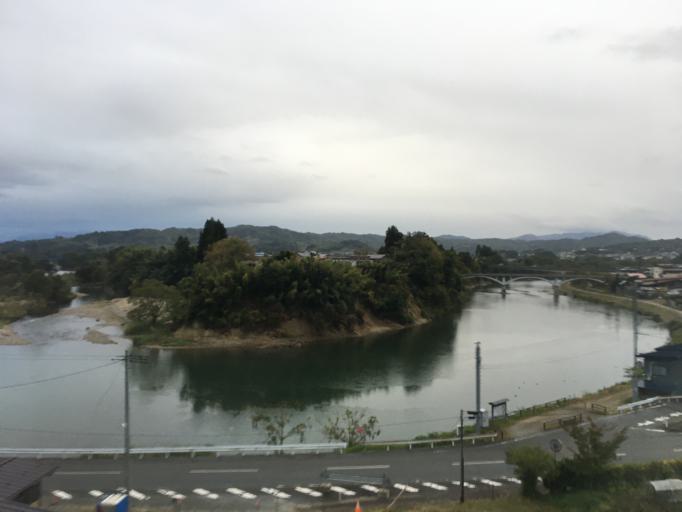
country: JP
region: Yamagata
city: Sagae
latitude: 38.3850
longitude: 140.2139
